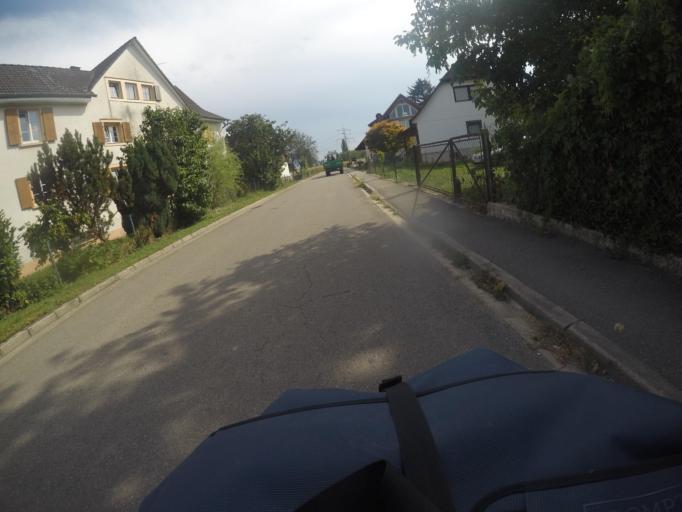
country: DE
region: Baden-Wuerttemberg
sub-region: Freiburg Region
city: Efringen-Kirchen
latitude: 47.6462
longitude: 7.5691
